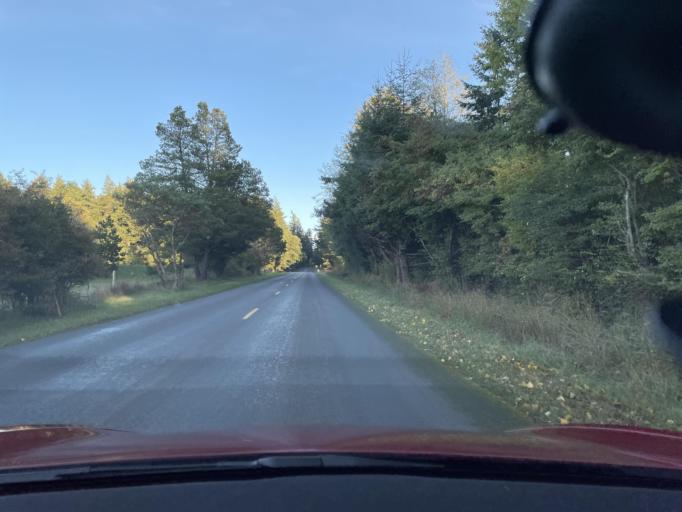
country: US
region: Washington
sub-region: San Juan County
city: Friday Harbor
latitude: 48.5651
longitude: -123.1590
